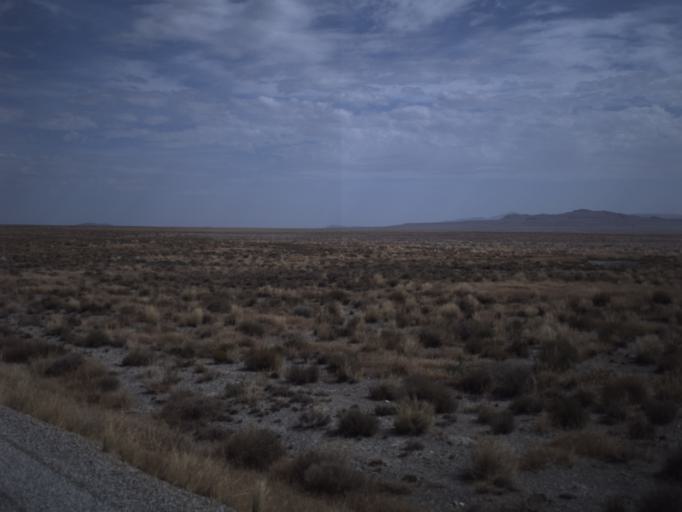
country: US
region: Utah
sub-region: Tooele County
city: Wendover
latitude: 41.4666
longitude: -113.6452
